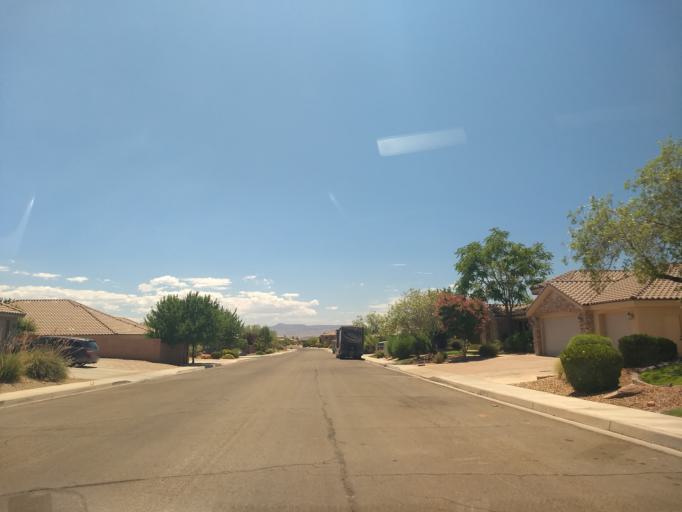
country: US
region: Utah
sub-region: Washington County
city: Washington
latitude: 37.1557
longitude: -113.5217
